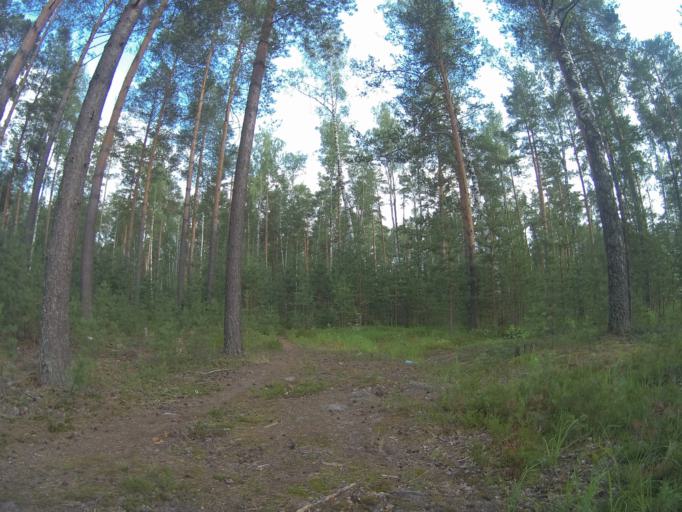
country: RU
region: Vladimir
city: Vorsha
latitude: 56.0082
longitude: 40.1320
